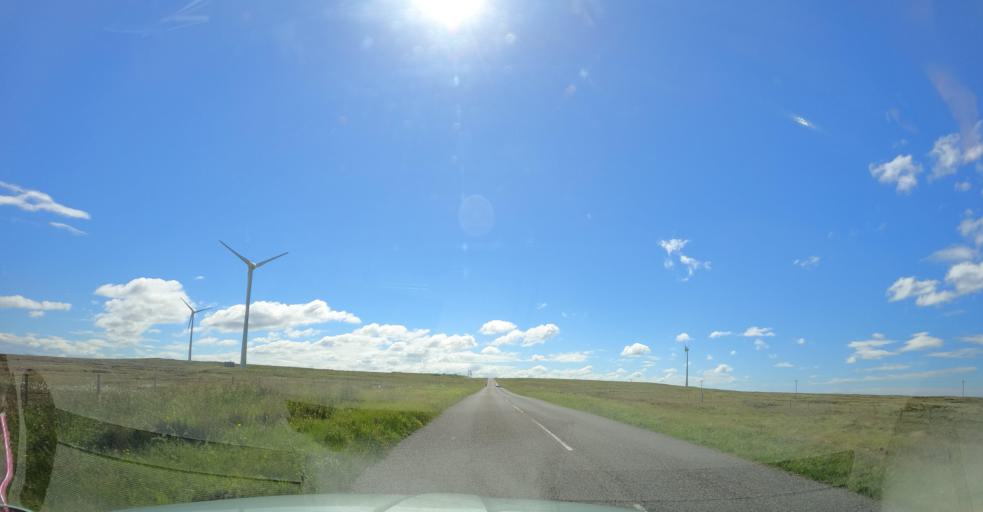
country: GB
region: Scotland
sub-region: Eilean Siar
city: Isle of Lewis
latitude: 58.3863
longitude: -6.4939
